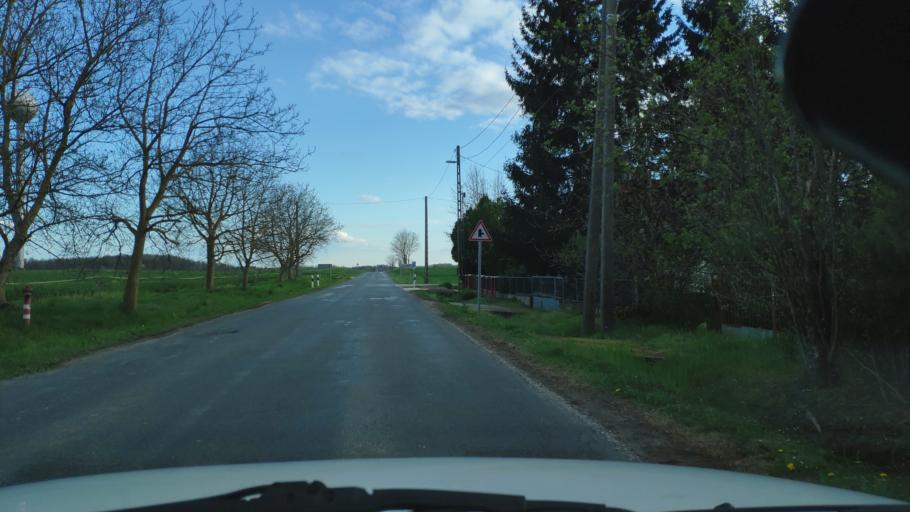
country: HU
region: Zala
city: Zalakomar
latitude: 46.4791
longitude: 17.1281
